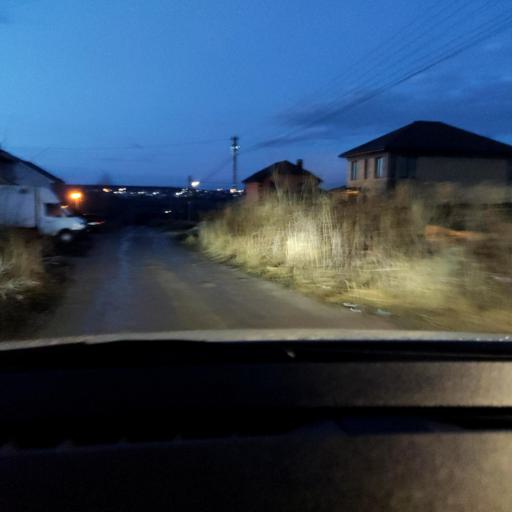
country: RU
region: Voronezj
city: Semiluki
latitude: 51.7131
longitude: 39.0208
